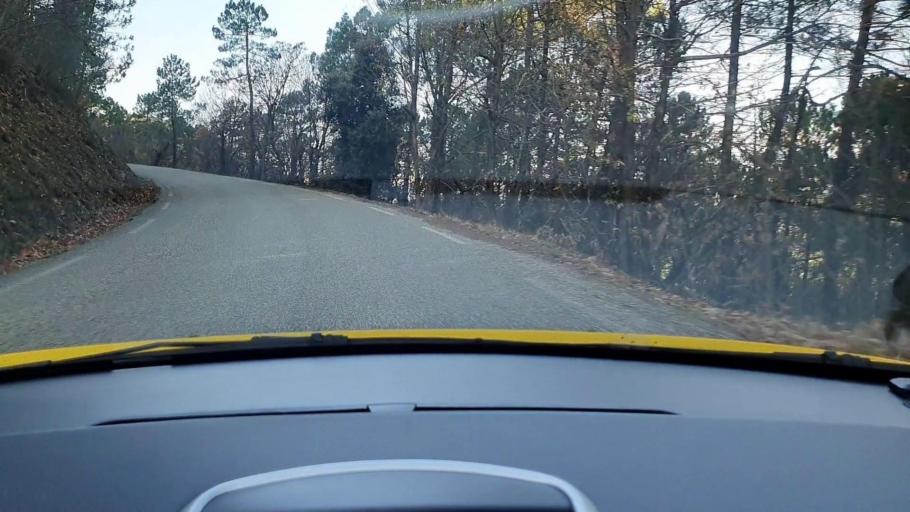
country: FR
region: Languedoc-Roussillon
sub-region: Departement du Gard
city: Branoux-les-Taillades
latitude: 44.2249
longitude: 3.9774
